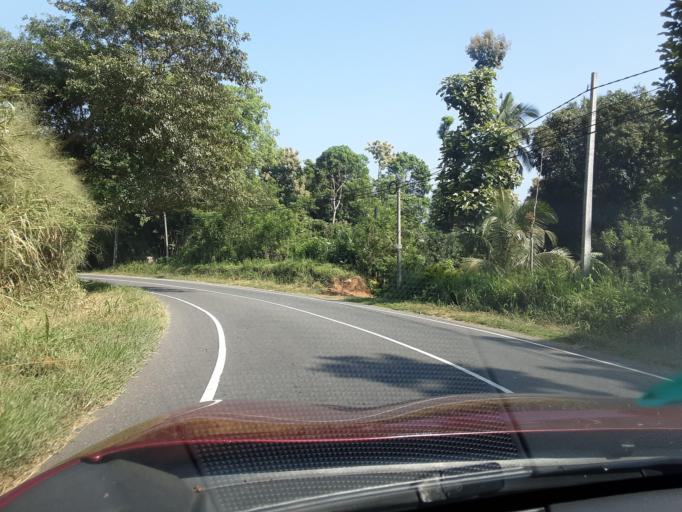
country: LK
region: Uva
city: Badulla
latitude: 7.1799
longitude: 81.0485
